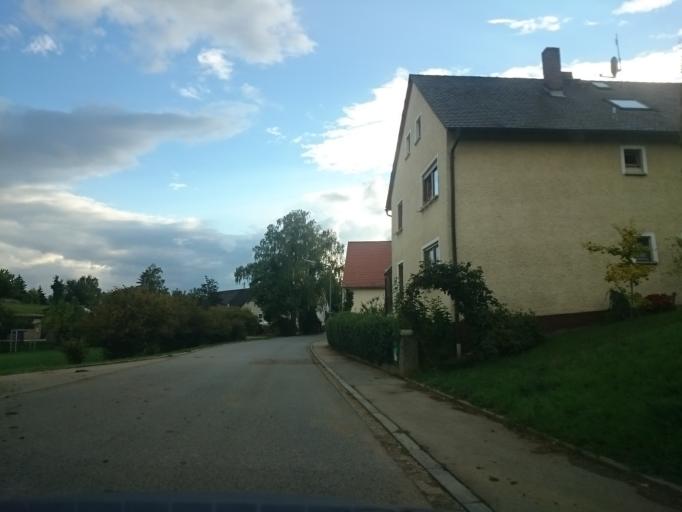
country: DE
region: Bavaria
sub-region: Regierungsbezirk Mittelfranken
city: Thalmassing
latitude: 49.1253
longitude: 11.1931
